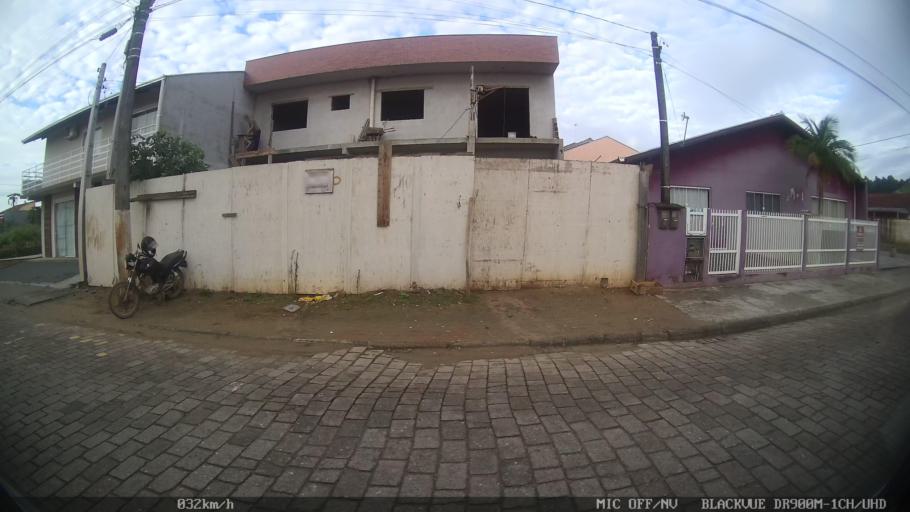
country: BR
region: Santa Catarina
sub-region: Barra Velha
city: Barra Velha
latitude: -26.6293
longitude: -48.6944
